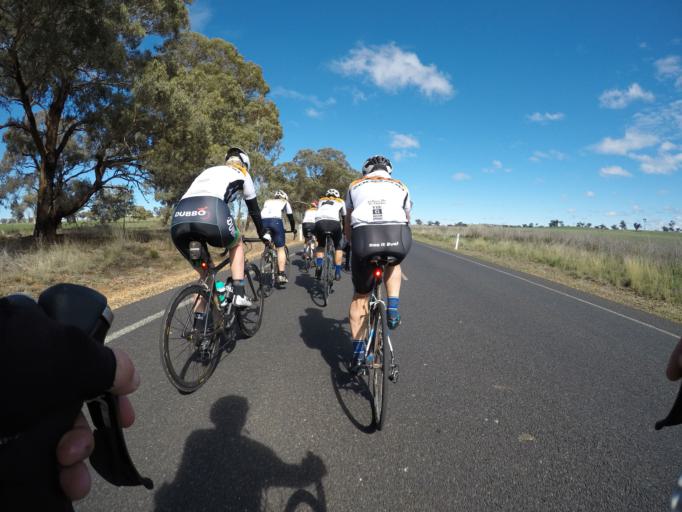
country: AU
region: New South Wales
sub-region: Wellington
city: Wellington
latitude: -32.7518
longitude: 148.6320
